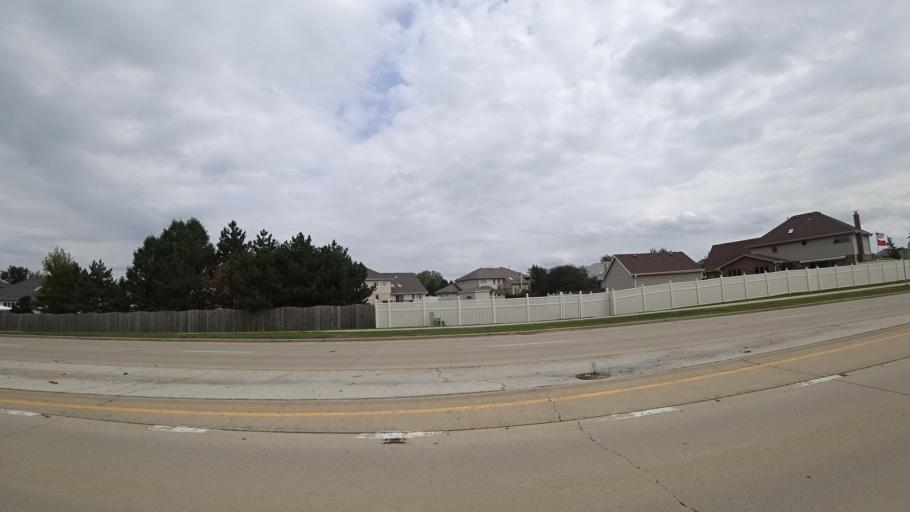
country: US
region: Illinois
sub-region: Cook County
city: Tinley Park
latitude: 41.5686
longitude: -87.8126
